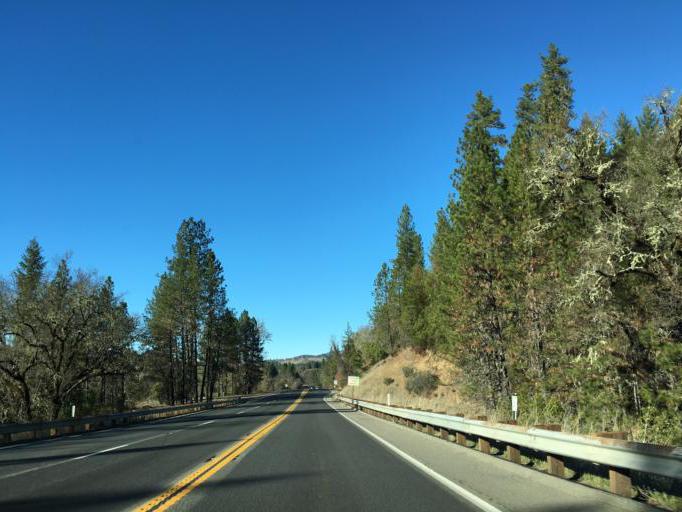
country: US
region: California
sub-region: Mendocino County
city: Laytonville
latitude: 39.7188
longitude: -123.5006
